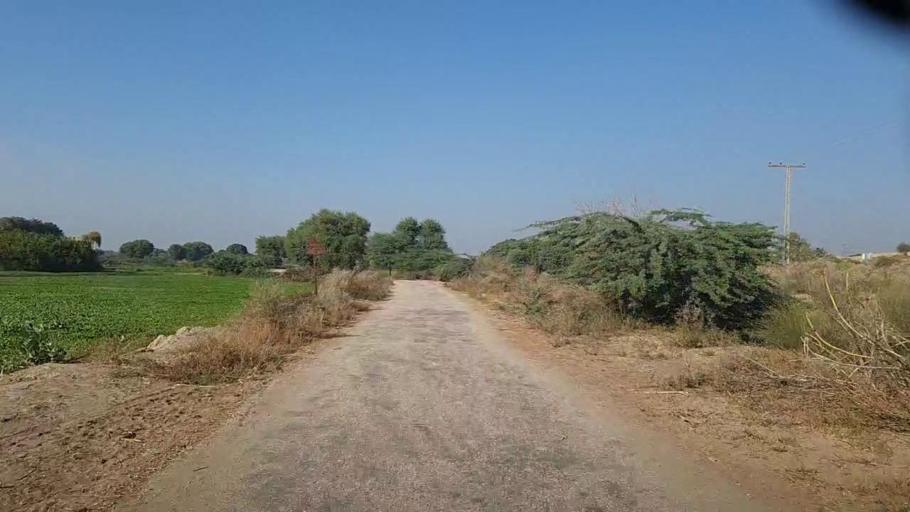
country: PK
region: Sindh
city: Darya Khan Marri
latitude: 26.6809
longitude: 68.3517
